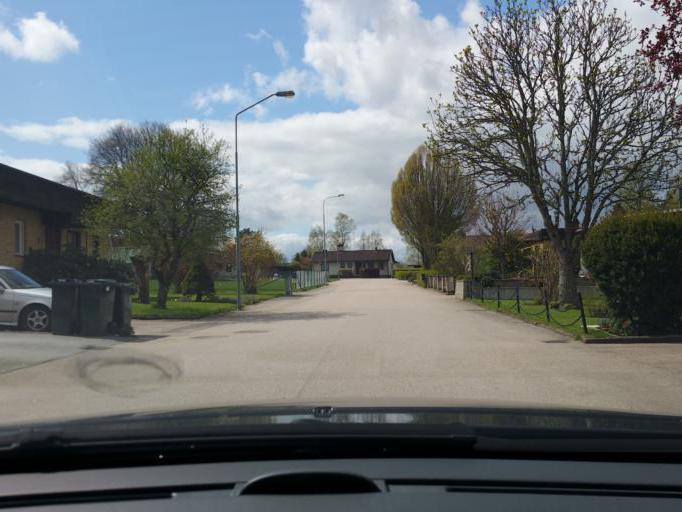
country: SE
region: Kronoberg
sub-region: Vaxjo Kommun
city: Lammhult
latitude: 57.1741
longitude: 14.5898
